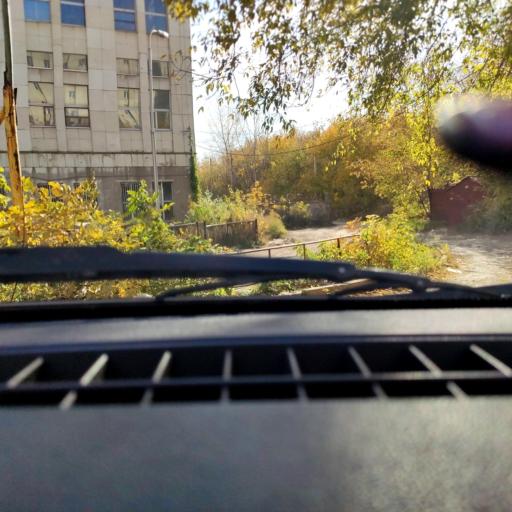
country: RU
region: Bashkortostan
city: Ufa
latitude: 54.7490
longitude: 56.0056
